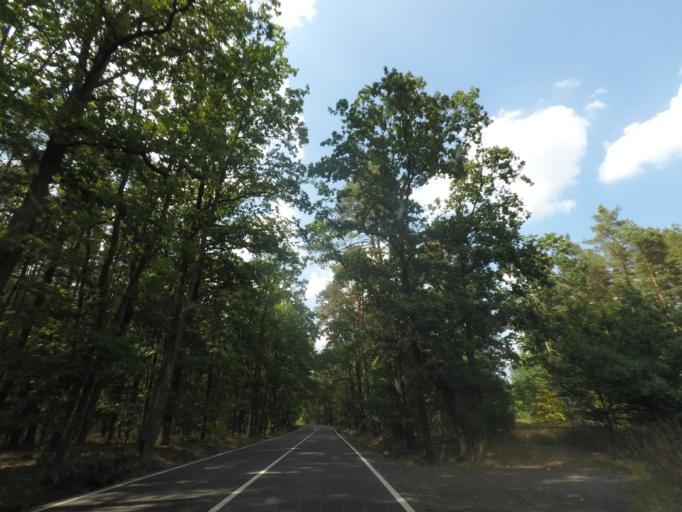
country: CZ
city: Borohradek
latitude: 50.1086
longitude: 16.0776
